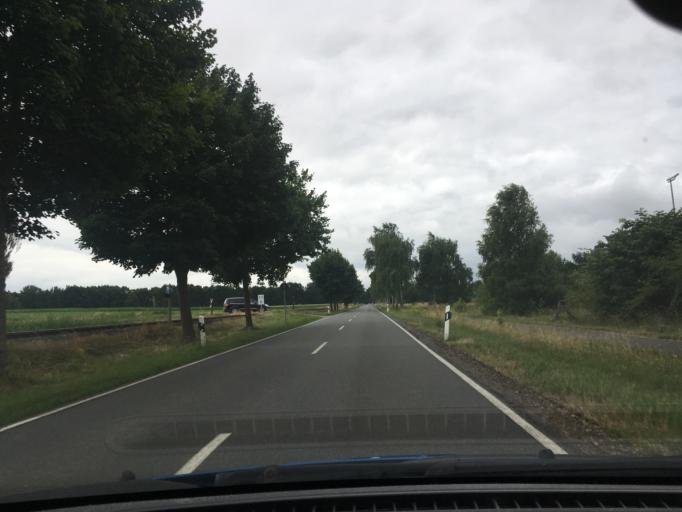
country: DE
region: Lower Saxony
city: Wulfsen
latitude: 53.2840
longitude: 10.1327
